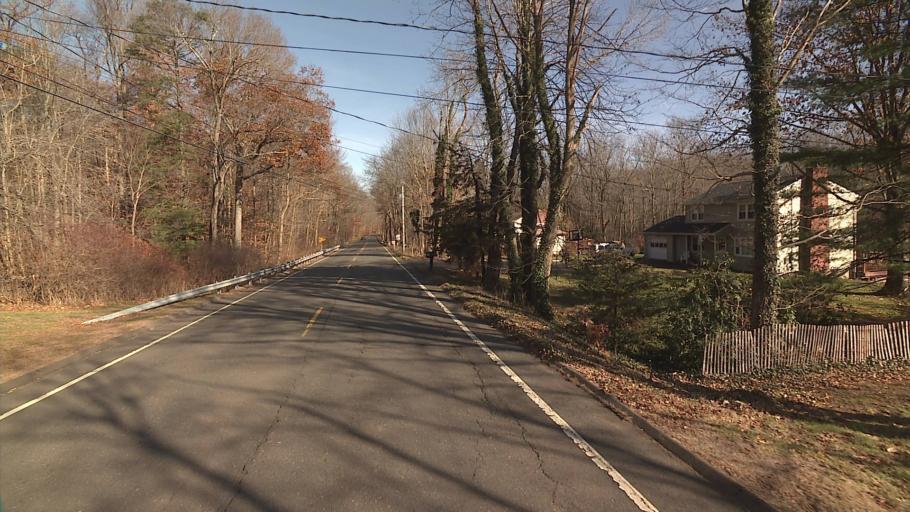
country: US
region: Connecticut
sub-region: Middlesex County
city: Durham
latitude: 41.4331
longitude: -72.7282
